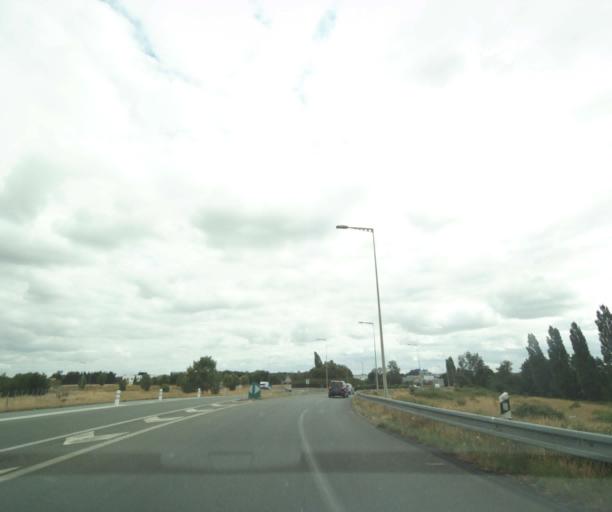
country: FR
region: Pays de la Loire
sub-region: Departement de Maine-et-Loire
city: Nuaille
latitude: 47.0820
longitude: -0.8305
